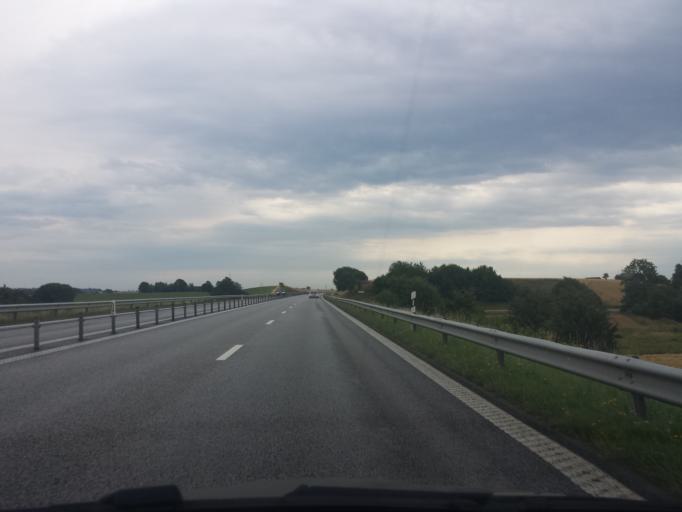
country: SE
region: Skane
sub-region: Skurups Kommun
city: Rydsgard
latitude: 55.4813
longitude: 13.6122
